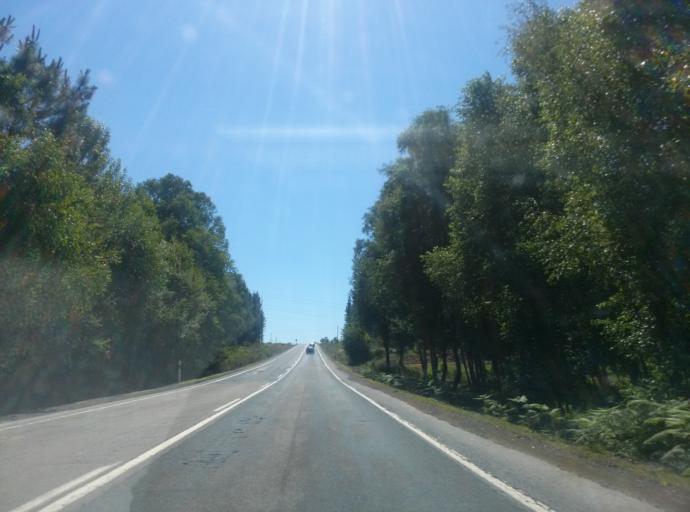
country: ES
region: Galicia
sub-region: Provincia de Lugo
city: Castro de Rei
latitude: 43.1336
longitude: -7.4119
